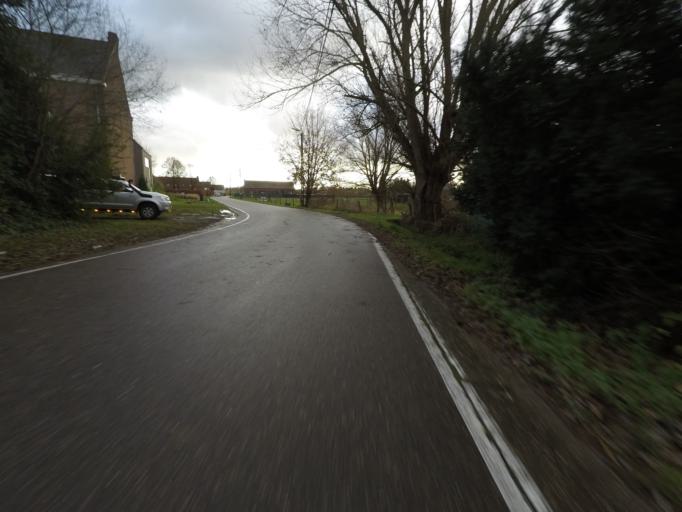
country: BE
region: Flanders
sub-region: Provincie Vlaams-Brabant
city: Begijnendijk
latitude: 51.0151
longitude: 4.7742
